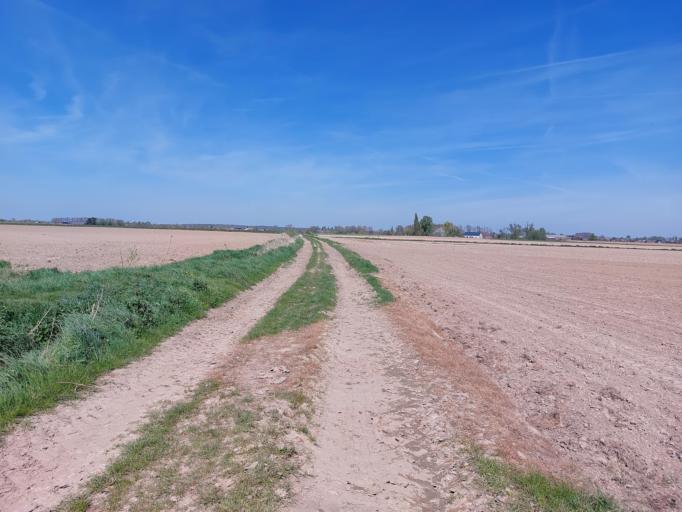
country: BE
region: Wallonia
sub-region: Province du Hainaut
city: Jurbise
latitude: 50.5483
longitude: 3.9382
